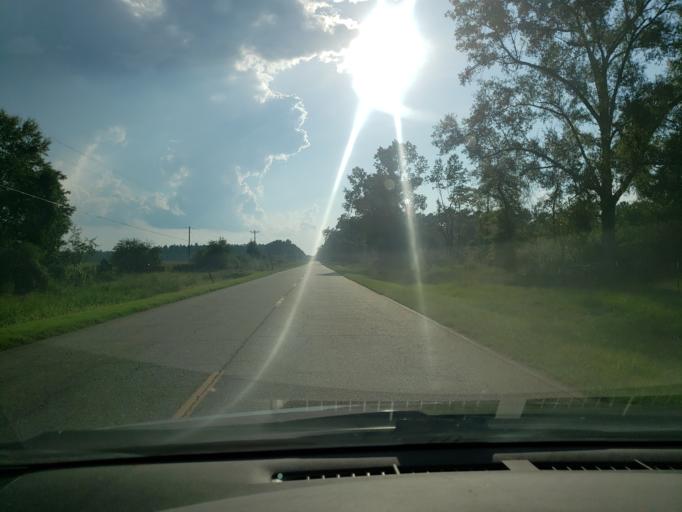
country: US
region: Georgia
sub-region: Dougherty County
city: Albany
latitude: 31.5736
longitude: -84.3182
